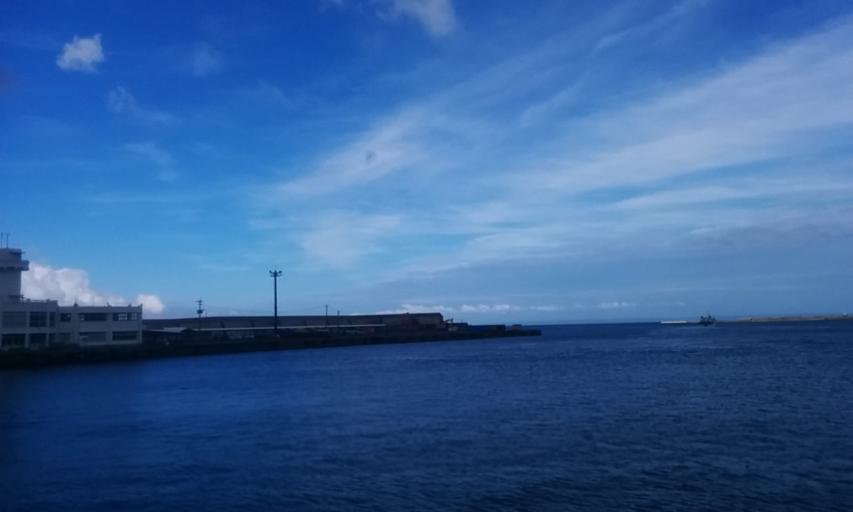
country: JP
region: Kagoshima
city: Nishinoomote
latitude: 30.4314
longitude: 130.5711
